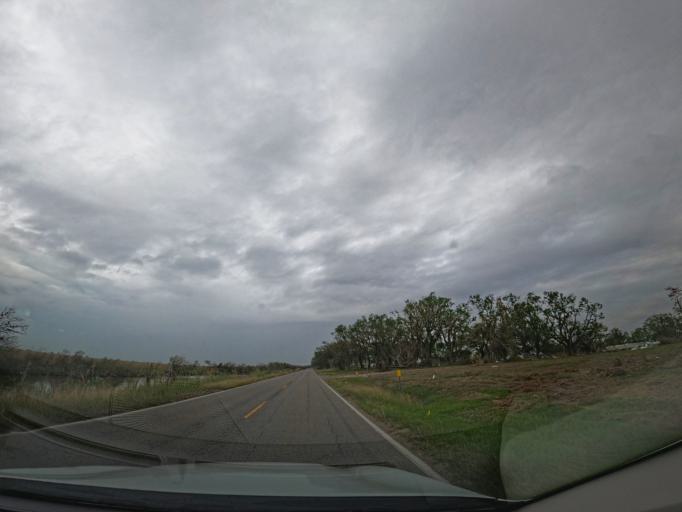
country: US
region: Louisiana
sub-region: Cameron Parish
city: Cameron
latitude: 29.7665
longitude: -92.9745
